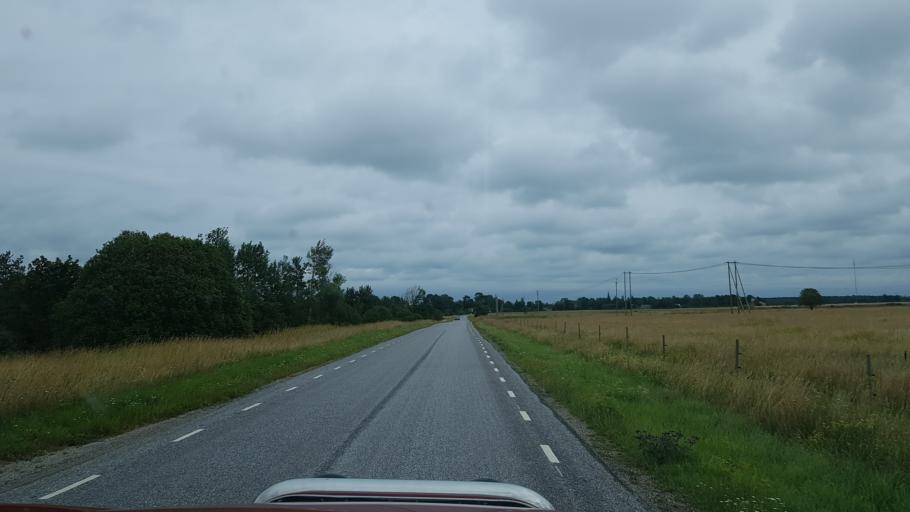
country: EE
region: Ida-Virumaa
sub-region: Puessi linn
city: Pussi
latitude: 59.3900
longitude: 27.0249
